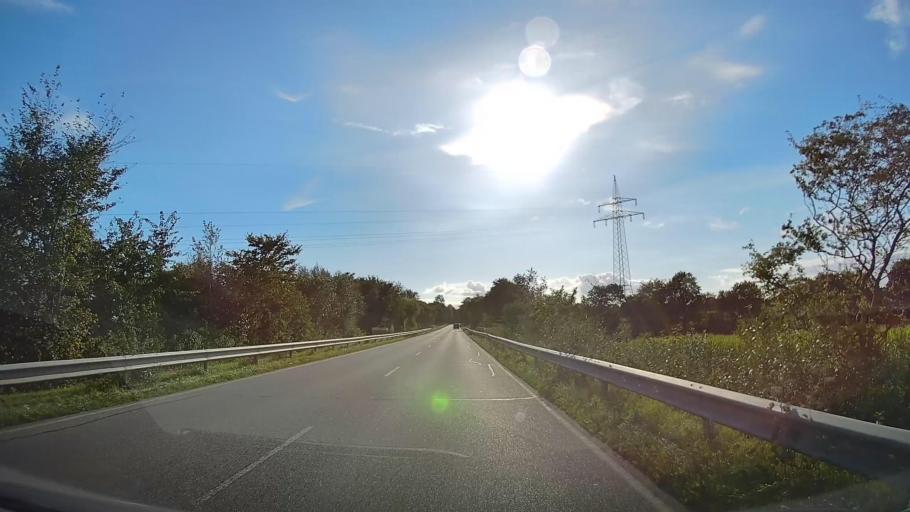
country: DE
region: Schleswig-Holstein
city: Thumby
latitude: 54.5644
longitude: 9.9448
